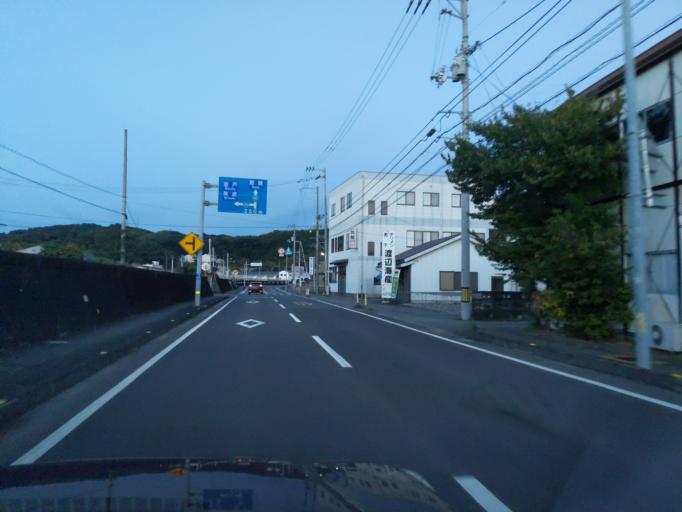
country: JP
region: Tokushima
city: Anan
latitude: 33.8722
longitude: 134.6402
